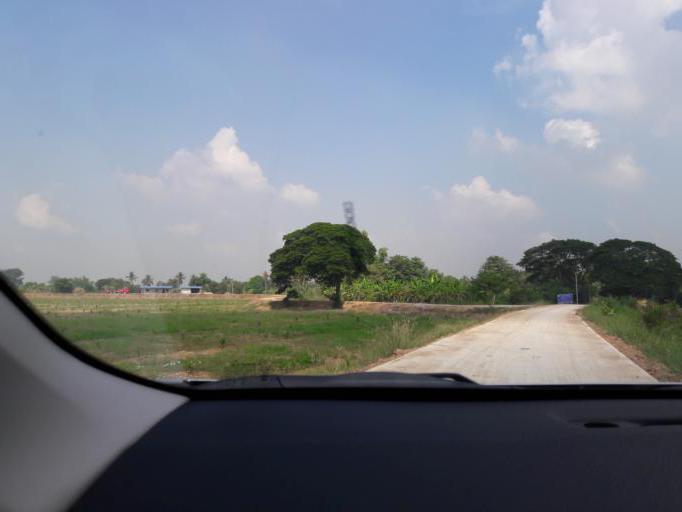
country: TH
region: Ang Thong
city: Ang Thong
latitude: 14.5640
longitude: 100.4142
